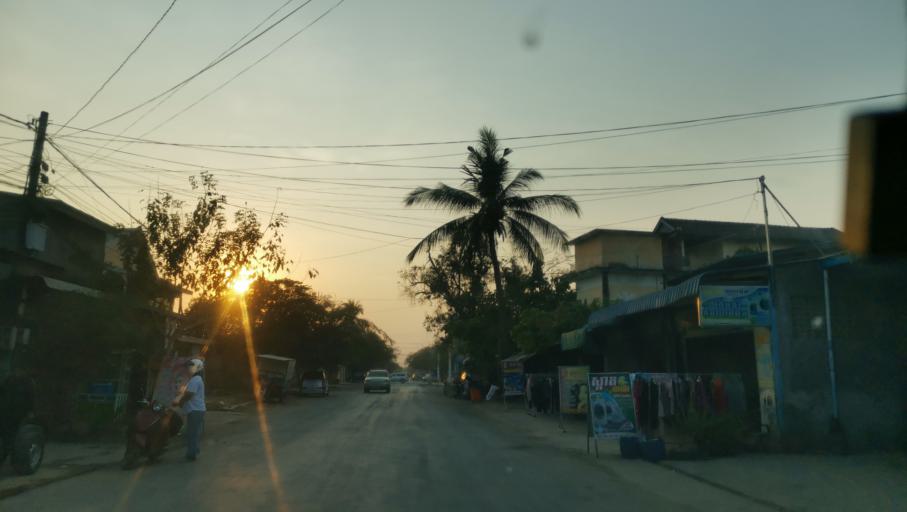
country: KH
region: Battambang
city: Battambang
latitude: 13.0850
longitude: 103.1984
